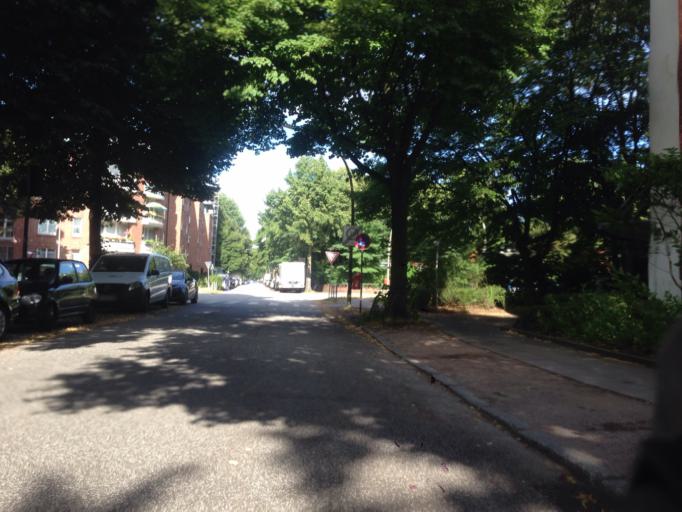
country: DE
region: Hamburg
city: Borgfelde
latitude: 53.5701
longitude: 10.0518
